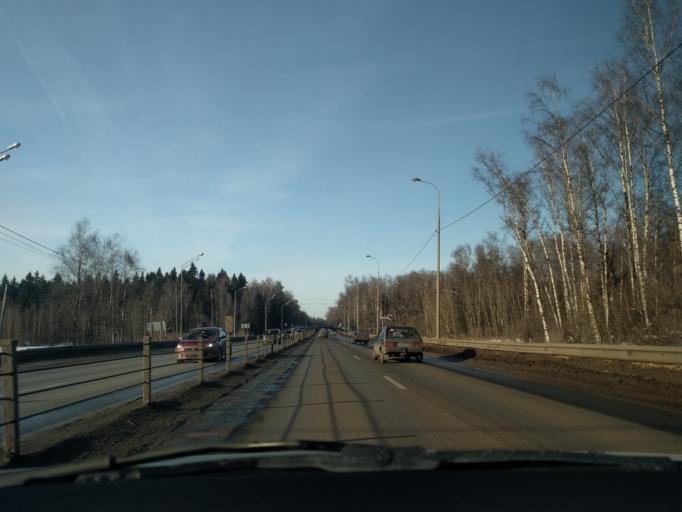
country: RU
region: Moskovskaya
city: Marfino
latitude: 56.0193
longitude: 37.5452
